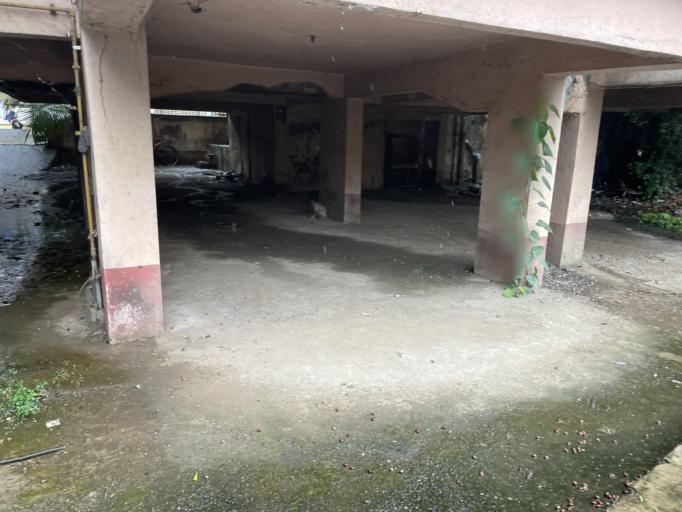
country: IN
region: Maharashtra
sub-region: Mumbai Suburban
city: Borivli
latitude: 19.2349
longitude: 72.8615
